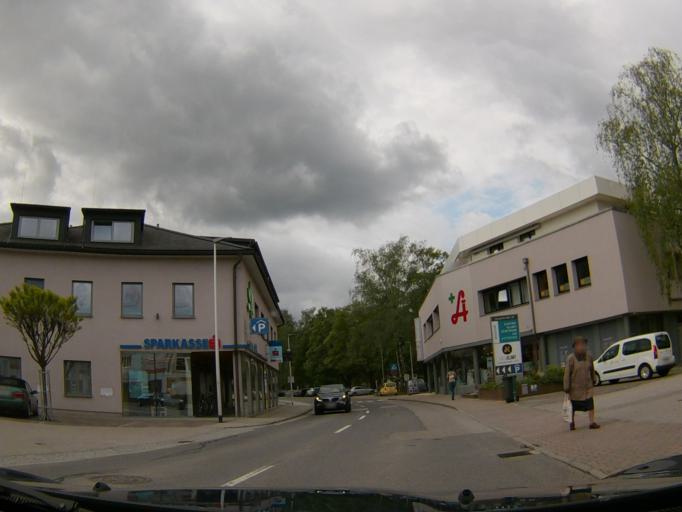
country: AT
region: Upper Austria
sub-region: Politischer Bezirk Vocklabruck
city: Seewalchen
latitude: 47.9466
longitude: 13.5948
